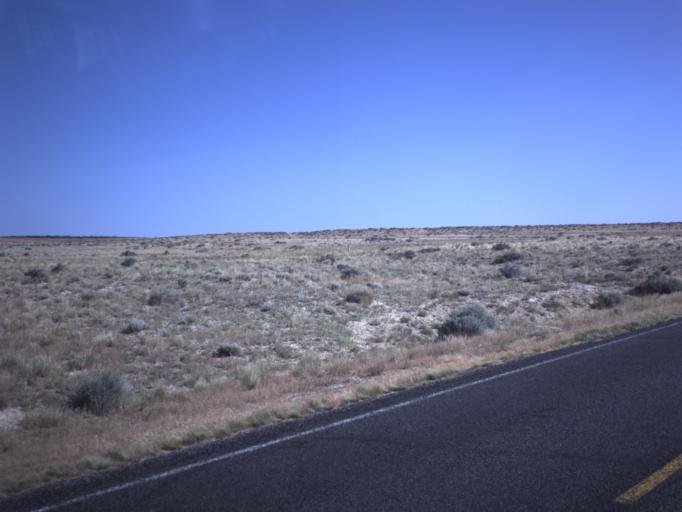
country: US
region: Utah
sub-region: Millard County
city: Fillmore
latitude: 38.9001
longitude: -112.8223
